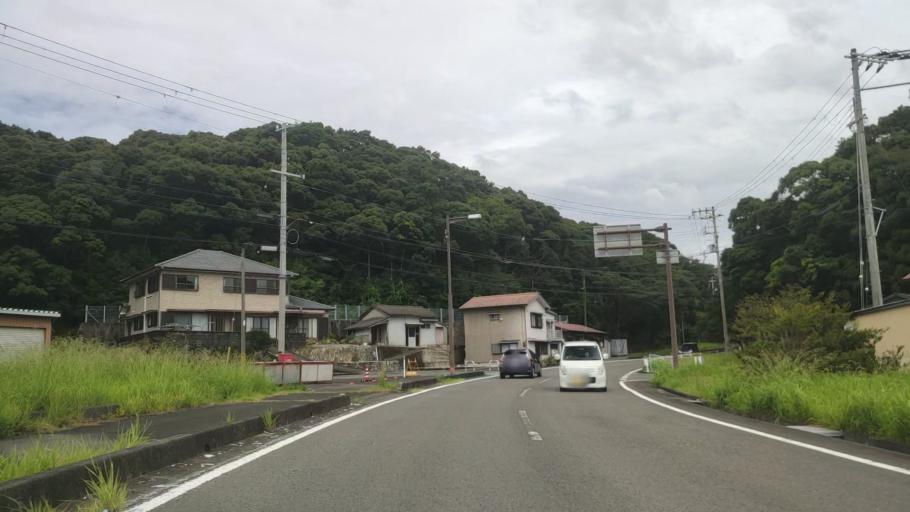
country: JP
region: Wakayama
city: Tanabe
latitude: 33.6809
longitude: 135.3887
